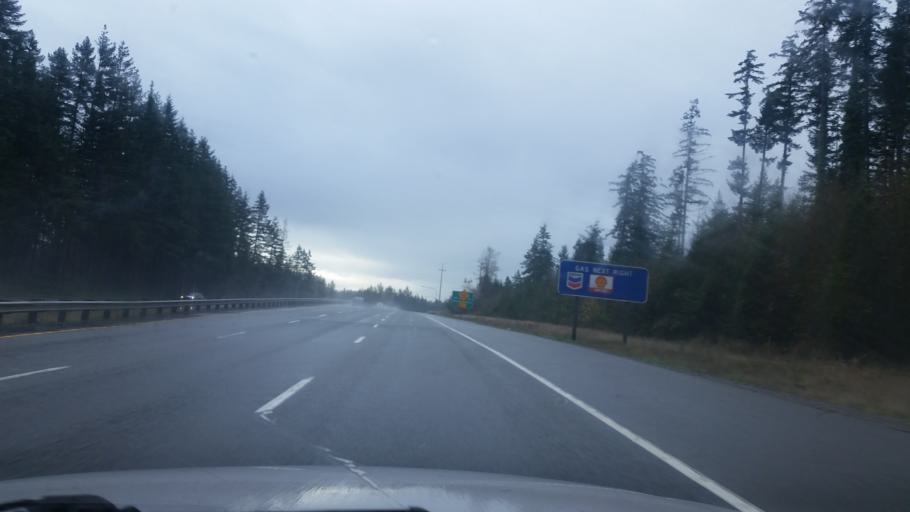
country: US
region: Washington
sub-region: King County
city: Maple Valley
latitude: 47.4015
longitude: -122.0448
